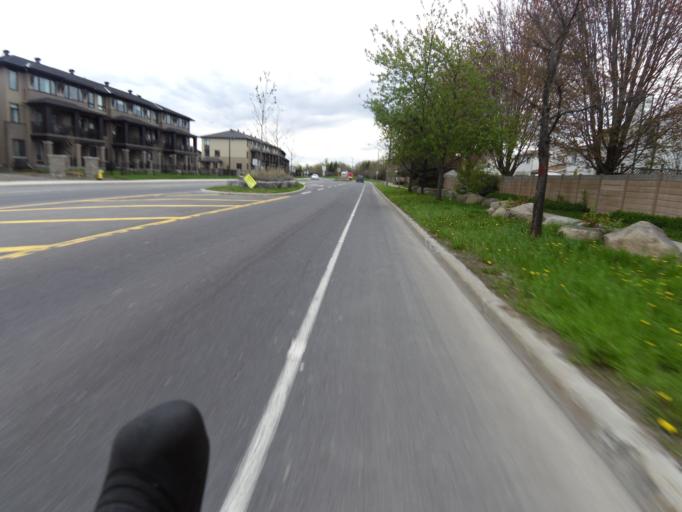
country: CA
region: Ontario
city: Bells Corners
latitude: 45.2876
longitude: -75.7366
